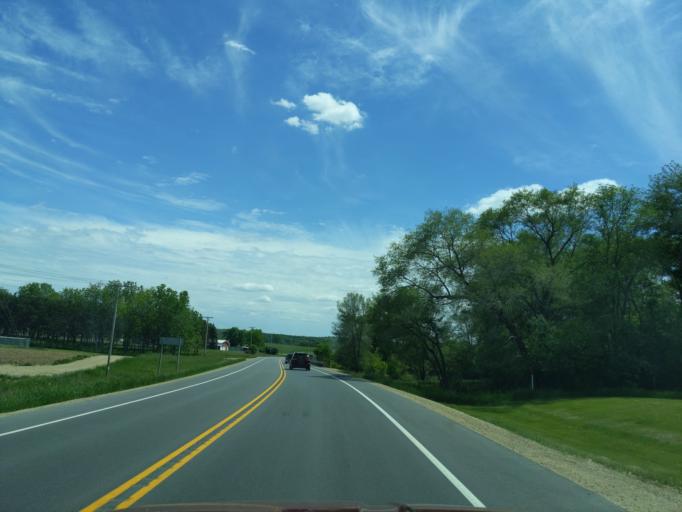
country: US
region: Wisconsin
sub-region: Columbia County
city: Pardeeville
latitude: 43.5089
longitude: -89.3067
